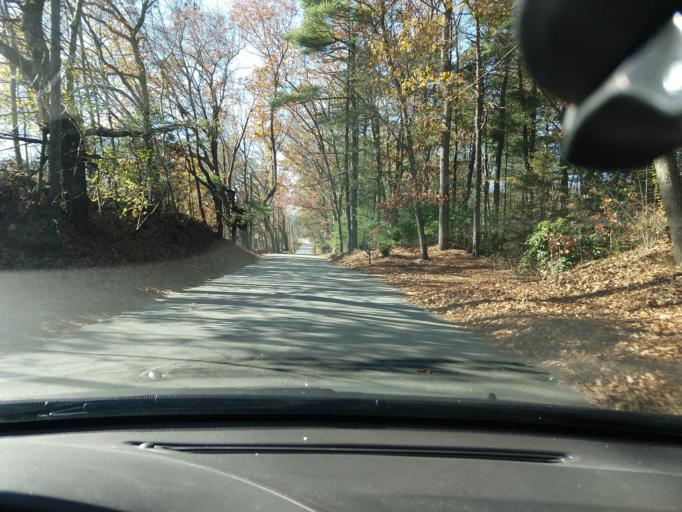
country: US
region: Massachusetts
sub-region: Middlesex County
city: Carlisle
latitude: 42.5097
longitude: -71.3203
